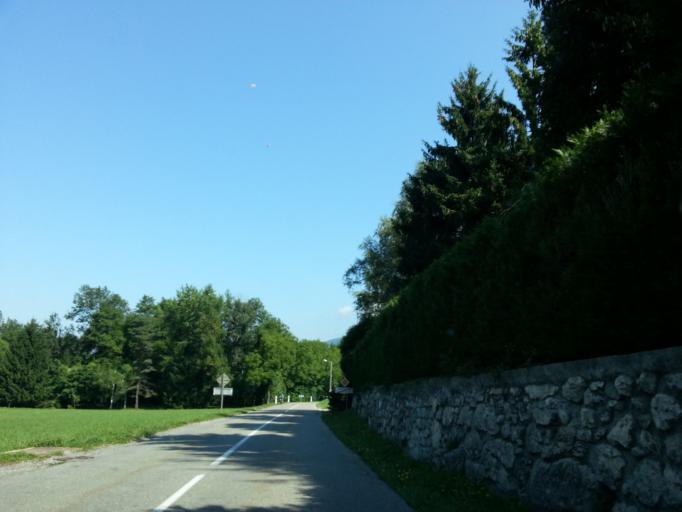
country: FR
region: Rhone-Alpes
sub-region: Departement de la Haute-Savoie
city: Doussard
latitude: 45.7905
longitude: 6.2316
